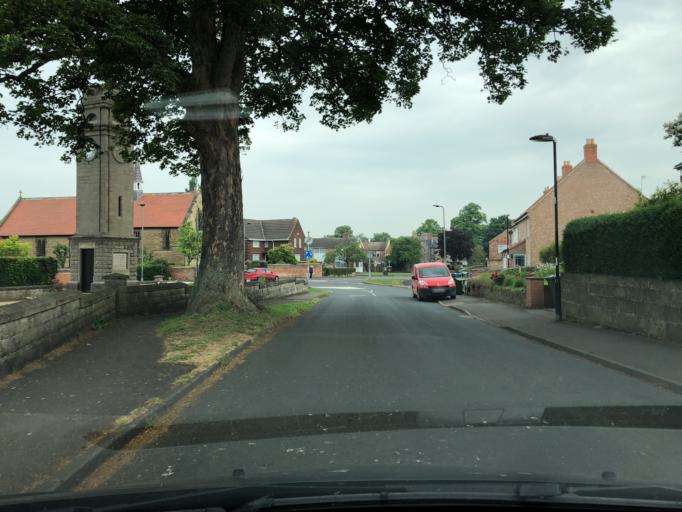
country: GB
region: England
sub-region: North Yorkshire
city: Northallerton
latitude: 54.3325
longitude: -1.4470
